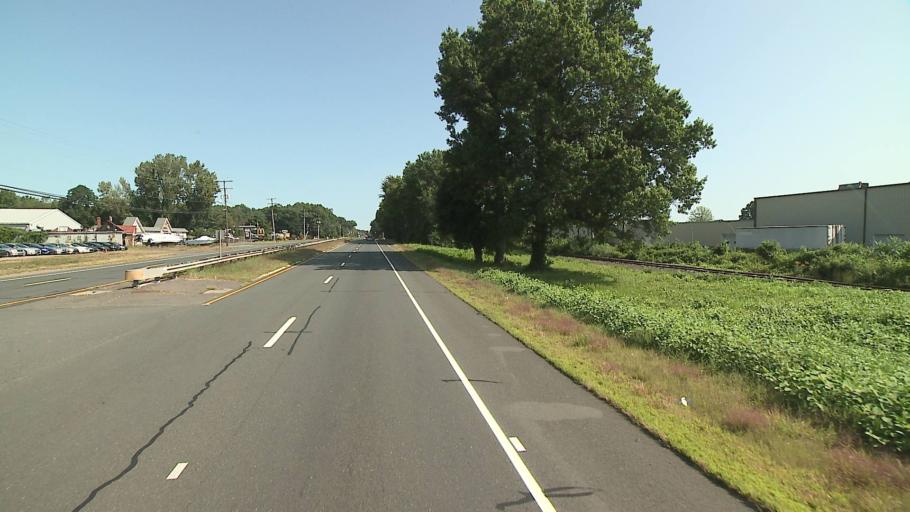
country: US
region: Connecticut
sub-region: Hartford County
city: South Windsor
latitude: 41.8218
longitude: -72.6084
